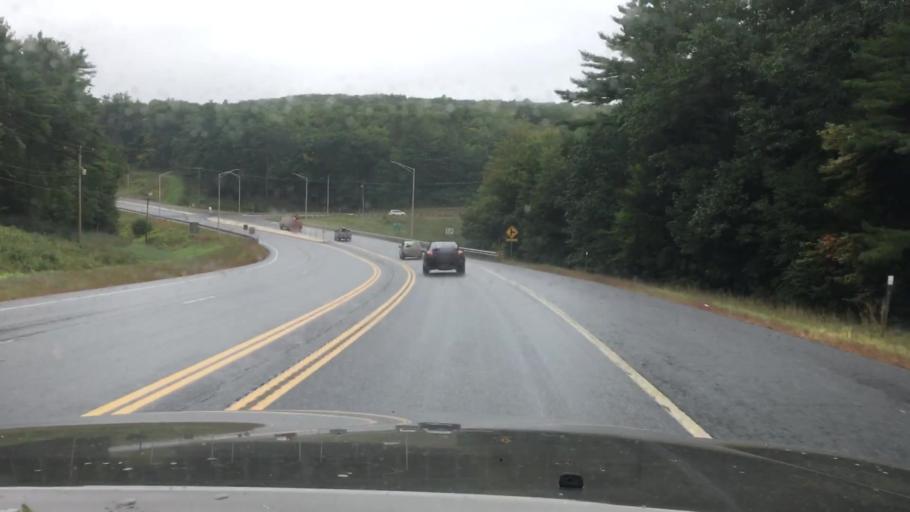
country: US
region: New Hampshire
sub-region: Cheshire County
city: Keene
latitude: 42.9684
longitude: -72.2582
